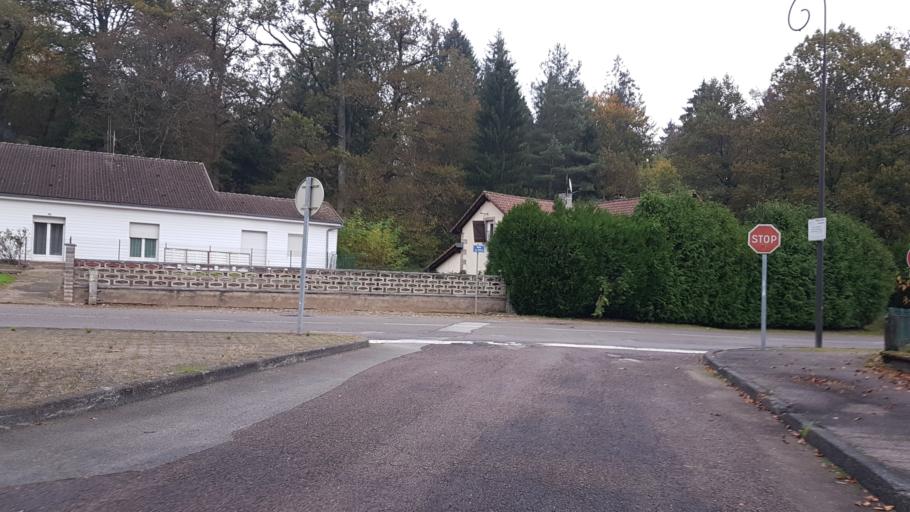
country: FR
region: Franche-Comte
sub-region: Departement de la Haute-Saone
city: Luxeuil-les-Bains
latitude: 47.8262
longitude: 6.3671
